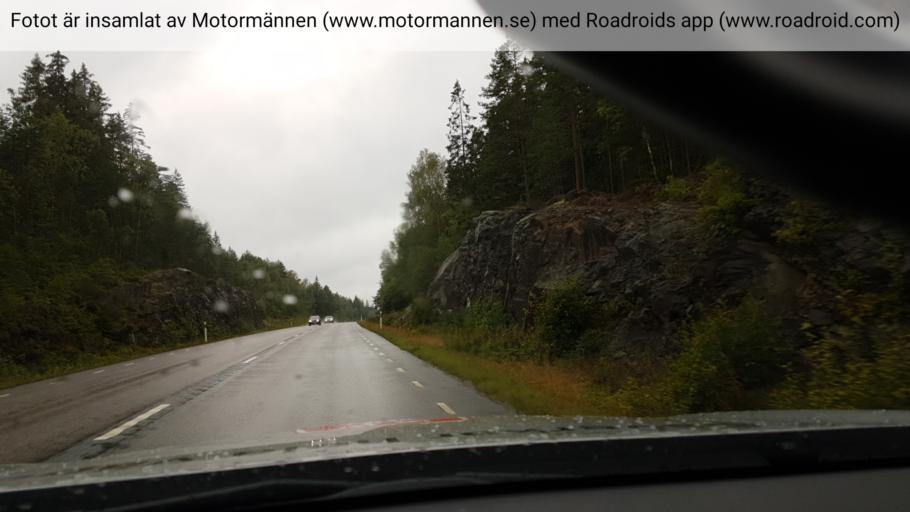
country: SE
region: Vaestra Goetaland
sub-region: Bengtsfors Kommun
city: Billingsfors
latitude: 58.9335
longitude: 12.1809
